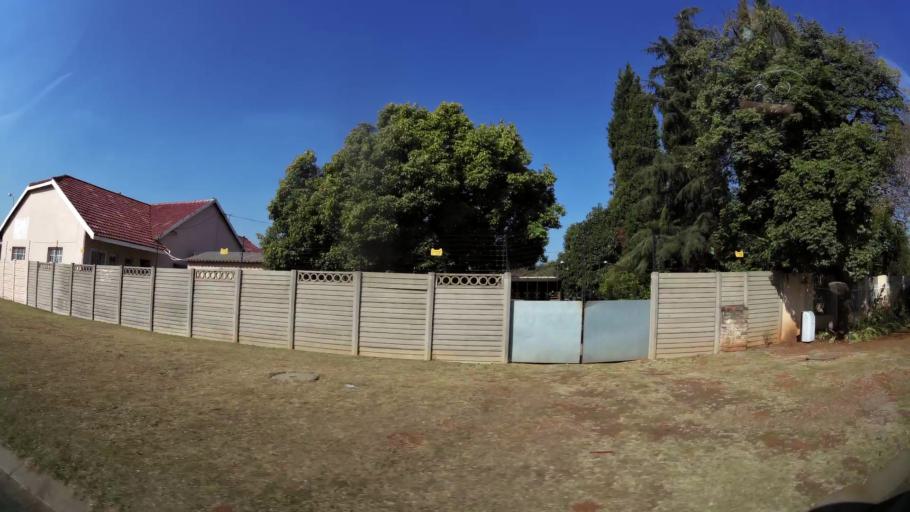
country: ZA
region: Gauteng
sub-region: West Rand District Municipality
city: Randfontein
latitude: -26.1791
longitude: 27.6924
